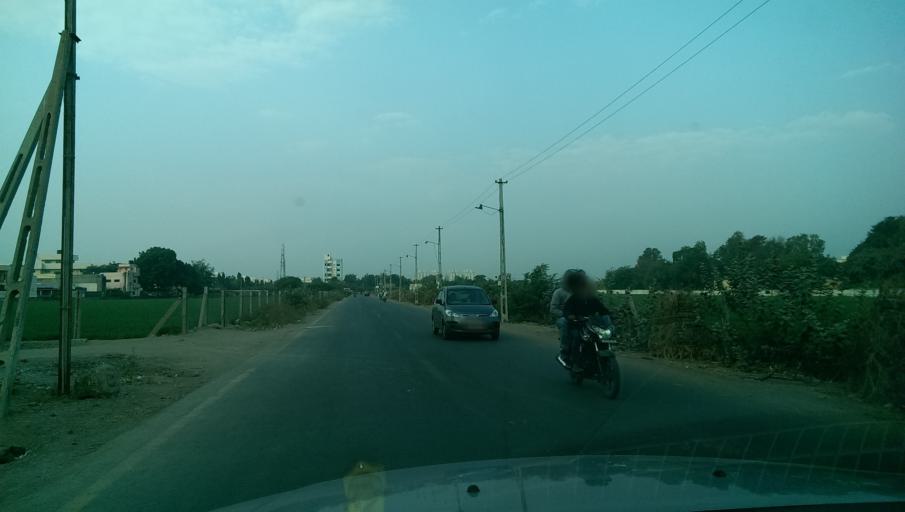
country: IN
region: Gujarat
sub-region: Jamnagar
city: Jamnagar
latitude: 22.4766
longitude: 70.0481
